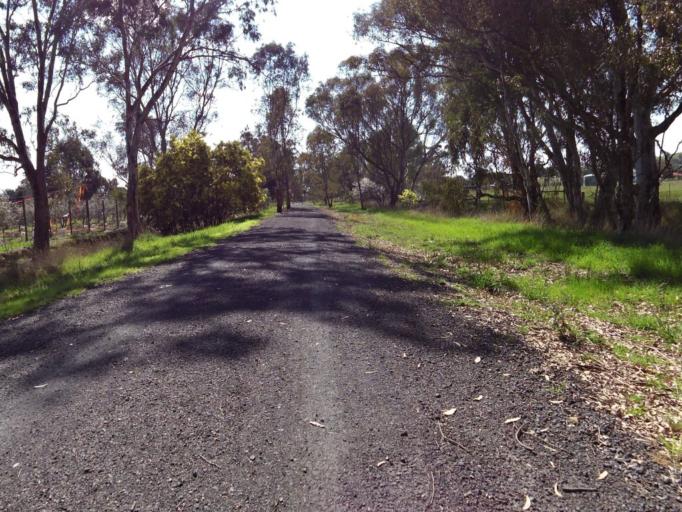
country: AU
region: Victoria
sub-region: Murrindindi
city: Alexandra
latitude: -37.1073
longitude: 145.6145
